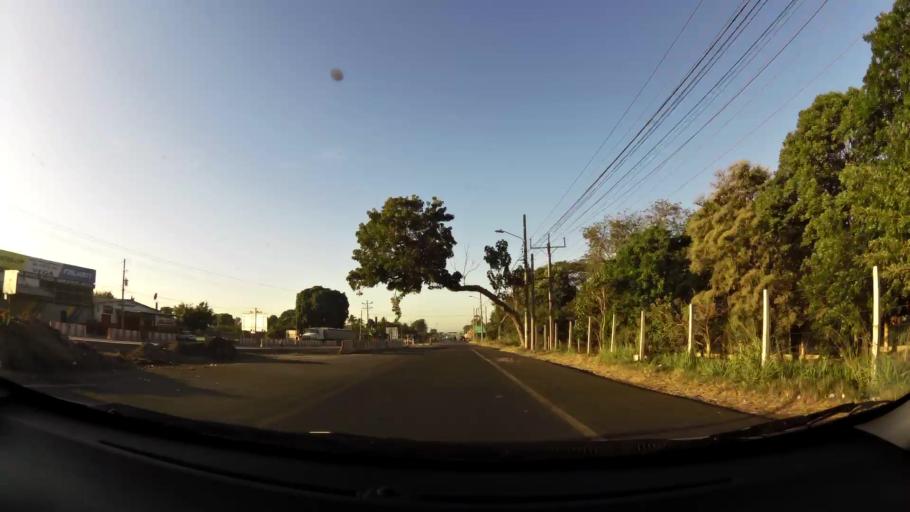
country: SV
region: Sonsonate
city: San Antonio del Monte
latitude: 13.7069
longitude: -89.7305
